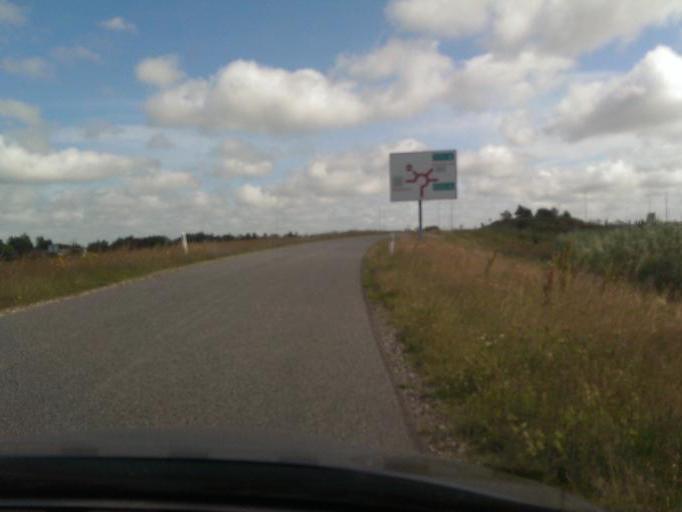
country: DK
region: North Denmark
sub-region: Bronderslev Kommune
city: Bronderslev
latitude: 57.2017
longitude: 9.9284
